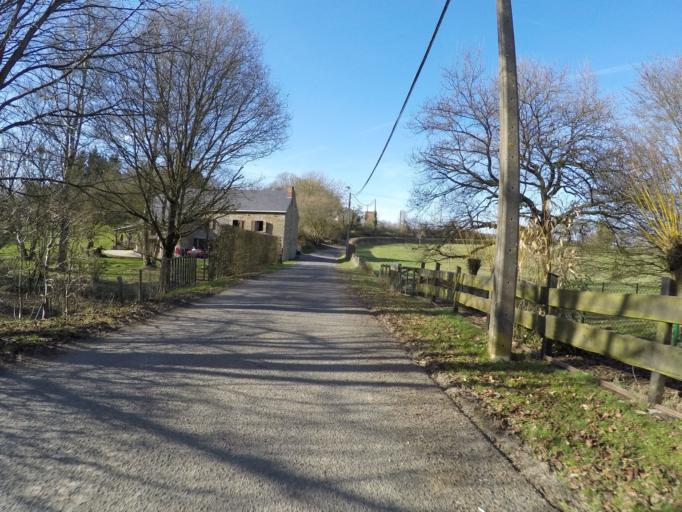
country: BE
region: Wallonia
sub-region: Province de Namur
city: Gesves
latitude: 50.3584
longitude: 5.0862
